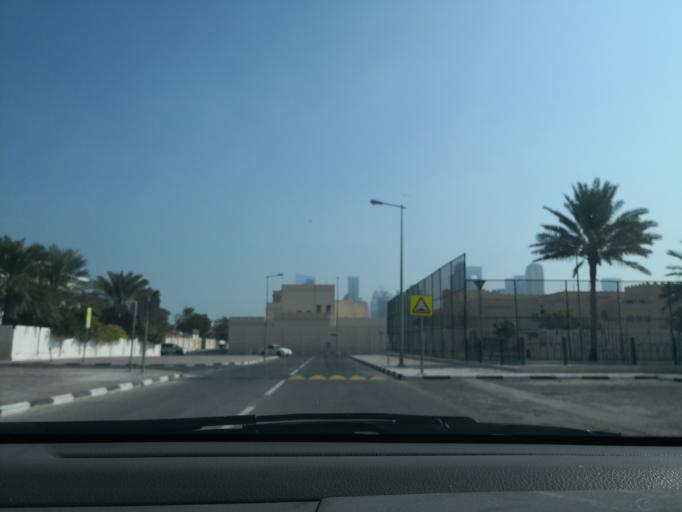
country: QA
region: Baladiyat ad Dawhah
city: Doha
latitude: 25.3296
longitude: 51.5099
